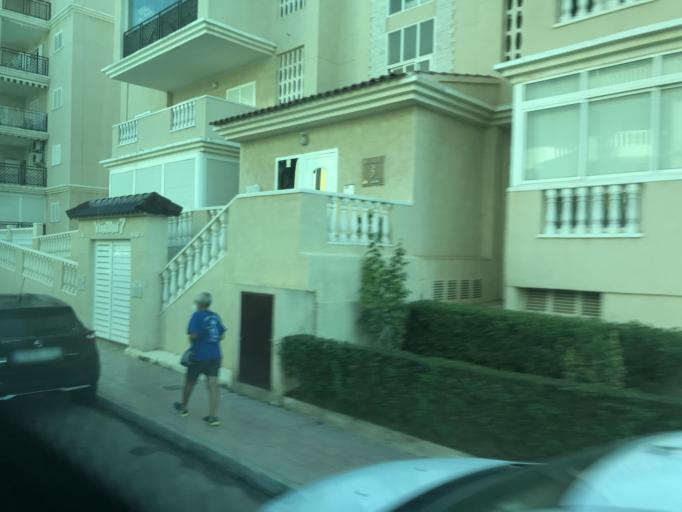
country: ES
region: Valencia
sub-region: Provincia de Alicante
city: Torrevieja
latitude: 38.0174
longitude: -0.6568
